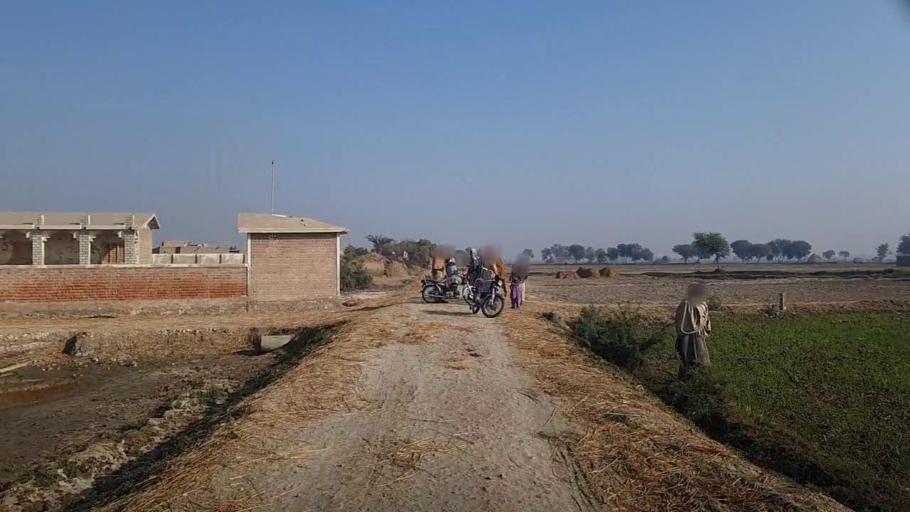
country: PK
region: Sindh
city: Radhan
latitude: 27.1177
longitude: 67.8958
